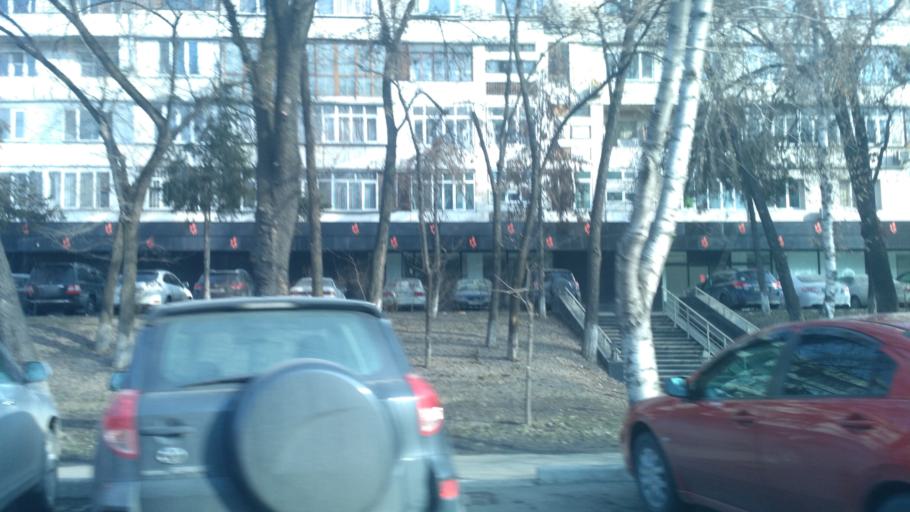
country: KZ
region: Almaty Qalasy
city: Almaty
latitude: 43.2269
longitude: 76.9208
